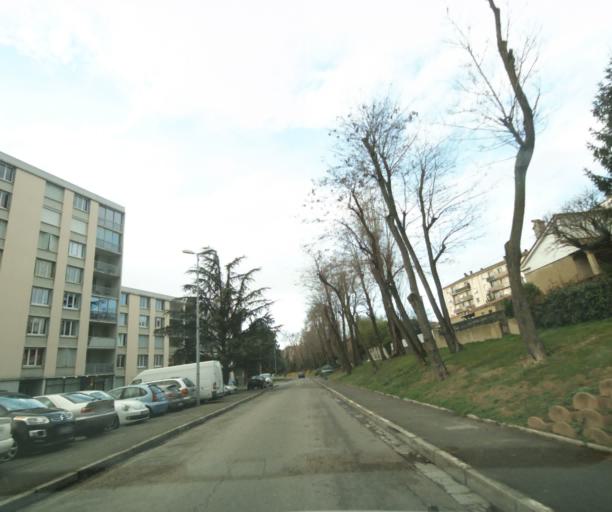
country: FR
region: Rhone-Alpes
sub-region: Departement de la Drome
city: Bourg-les-Valence
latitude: 44.9528
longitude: 4.9015
